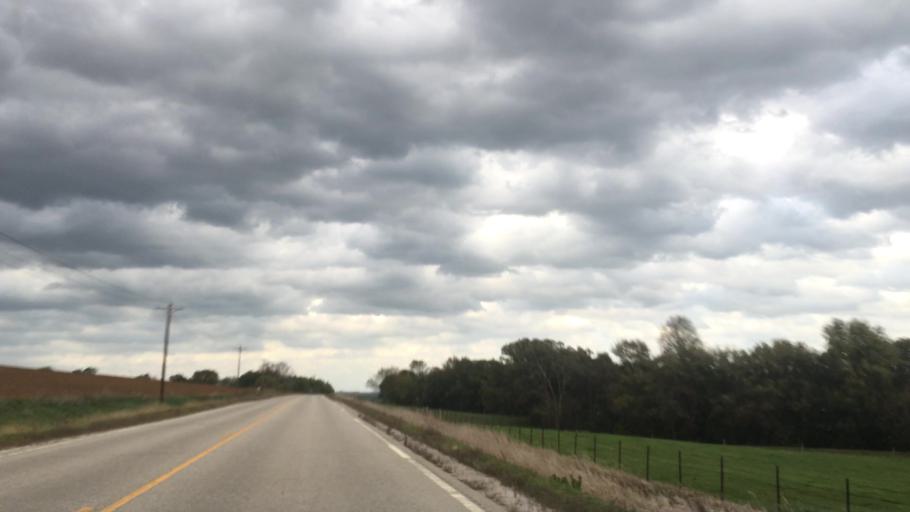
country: US
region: Minnesota
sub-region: Fillmore County
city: Preston
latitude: 43.7348
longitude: -92.0137
